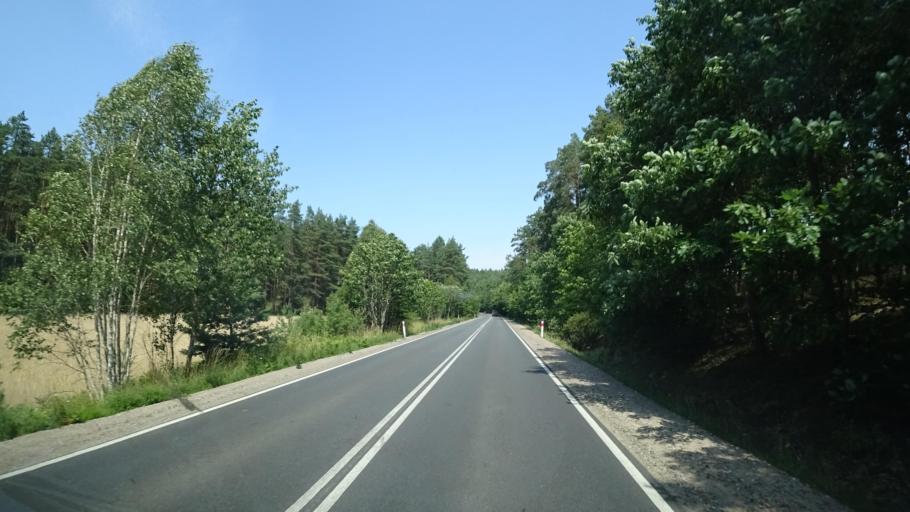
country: PL
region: Pomeranian Voivodeship
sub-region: Powiat koscierski
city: Dziemiany
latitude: 53.9805
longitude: 17.7737
